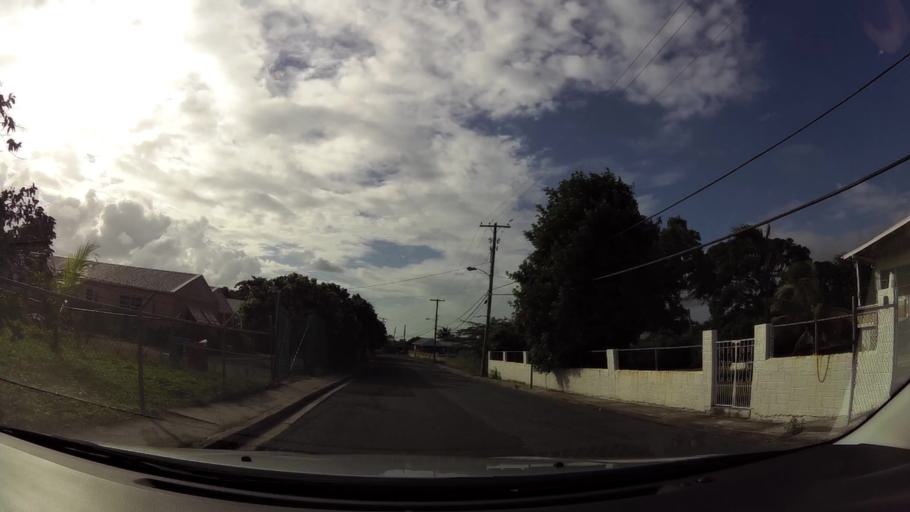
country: AG
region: Saint John
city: Saint John's
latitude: 17.1257
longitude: -61.8338
